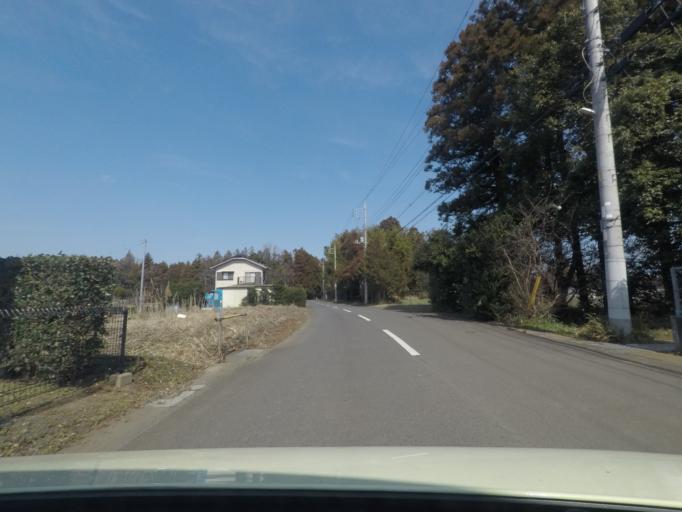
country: JP
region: Ibaraki
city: Okunoya
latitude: 36.1913
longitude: 140.3971
